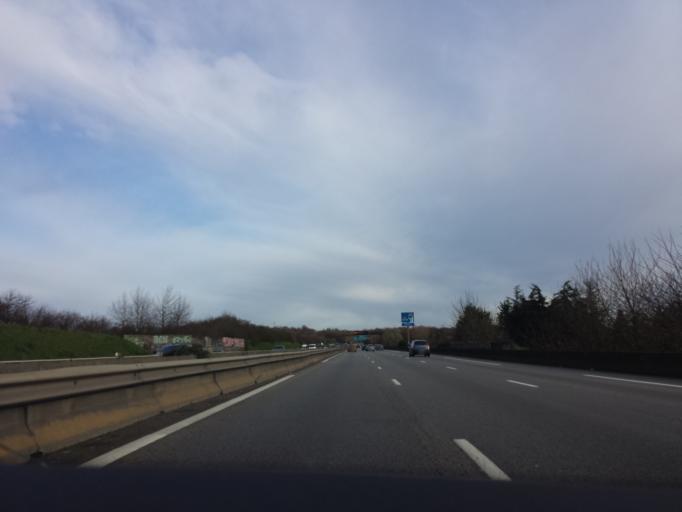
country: FR
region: Ile-de-France
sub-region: Departement des Yvelines
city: Bailly
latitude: 48.8323
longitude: 2.0841
